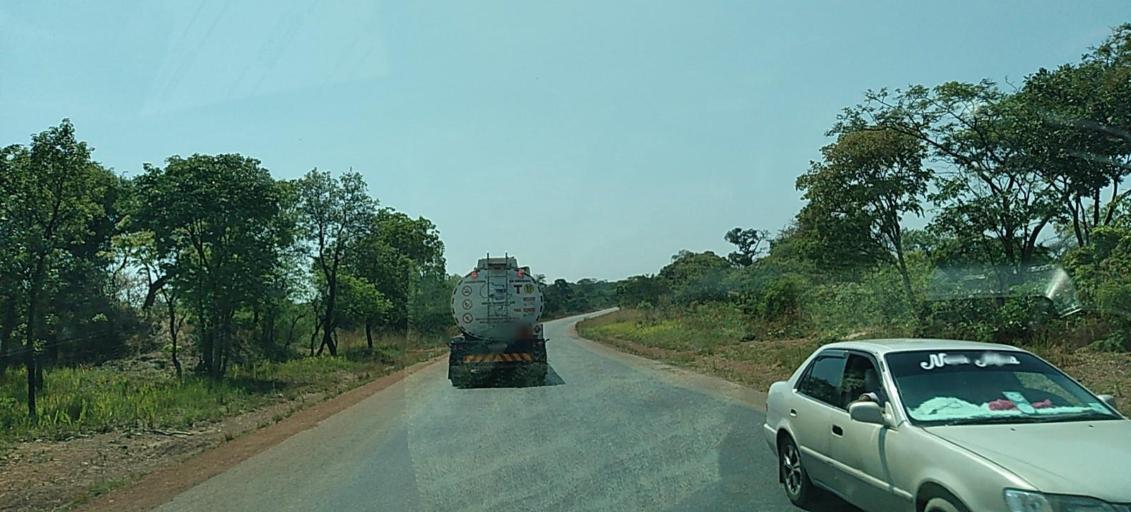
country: ZM
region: North-Western
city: Solwezi
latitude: -12.3623
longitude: 25.9704
